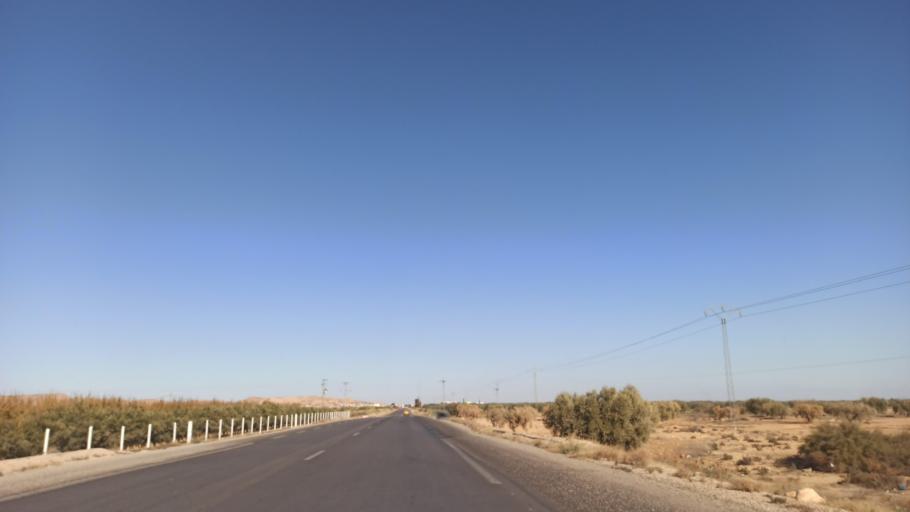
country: TN
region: Sidi Bu Zayd
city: Bi'r al Hufayy
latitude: 34.8931
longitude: 9.1703
